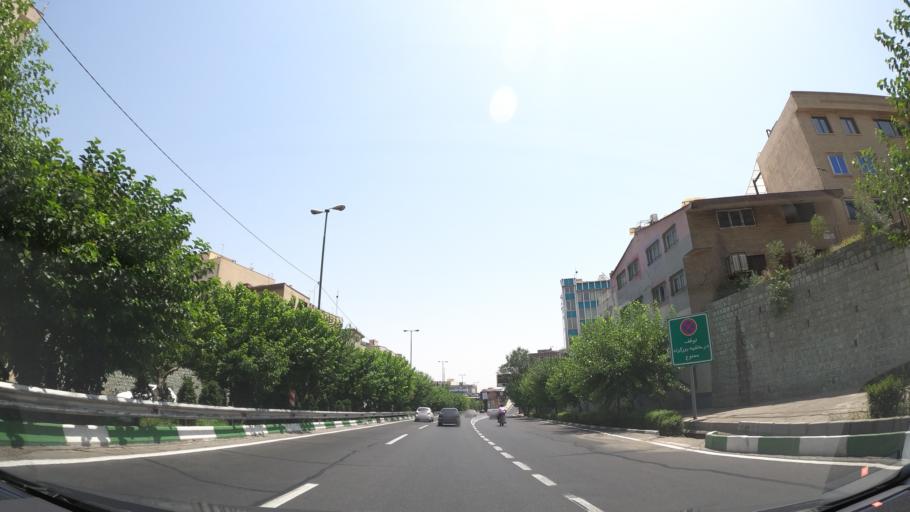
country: IR
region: Tehran
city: Tehran
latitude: 35.7260
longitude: 51.4242
